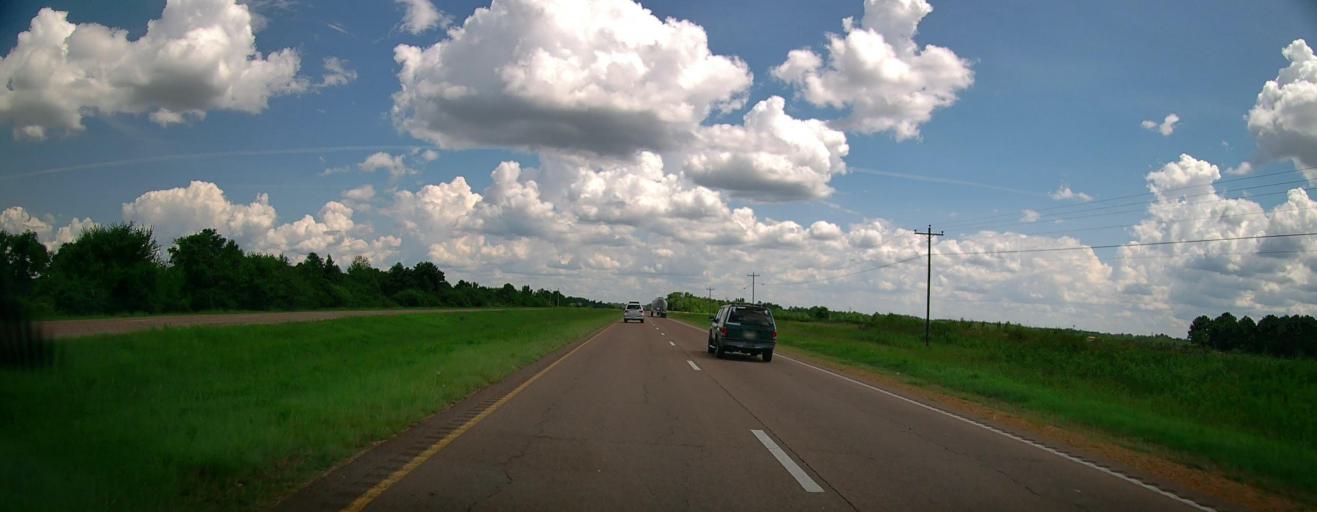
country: US
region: Mississippi
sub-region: Lowndes County
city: Columbus Air Force Base
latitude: 33.6930
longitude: -88.4402
